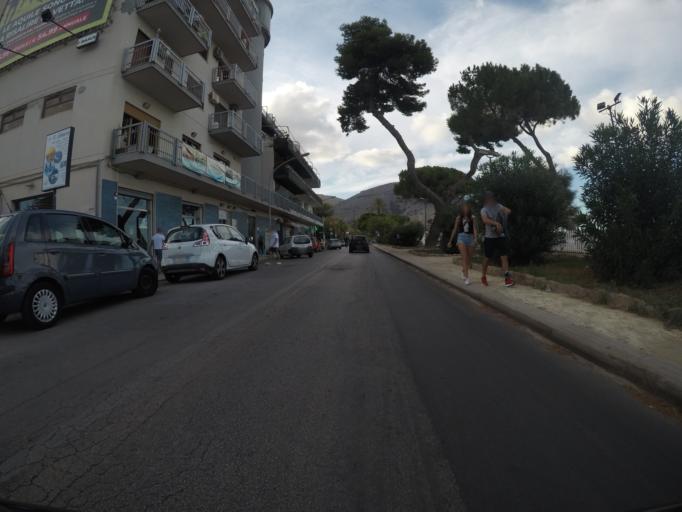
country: IT
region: Sicily
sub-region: Palermo
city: Palermo
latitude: 38.1978
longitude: 13.3306
